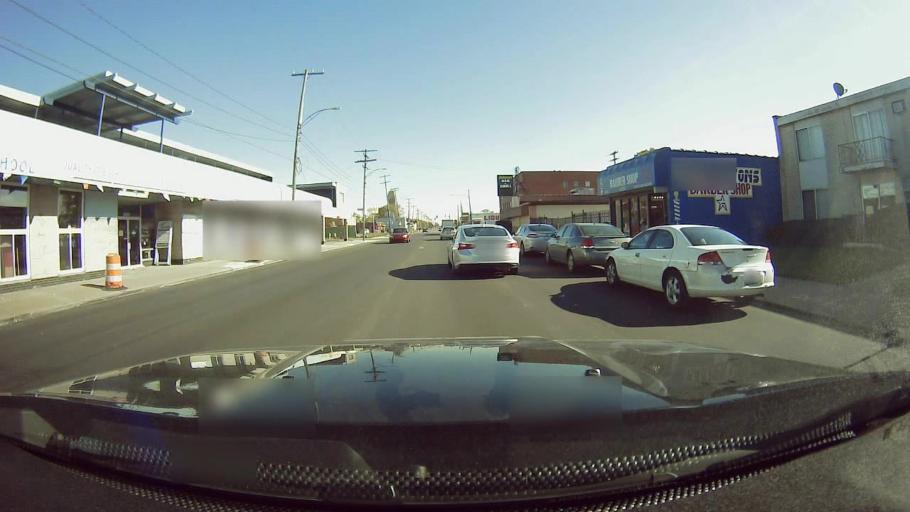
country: US
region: Michigan
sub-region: Wayne County
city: Dearborn
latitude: 42.3729
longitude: -83.1916
